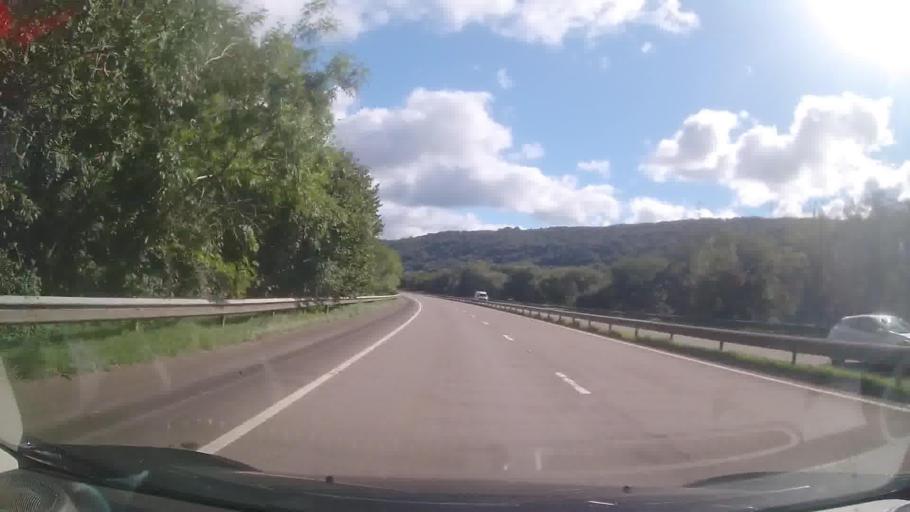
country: GB
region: Wales
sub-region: Neath Port Talbot
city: Neath
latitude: 51.6818
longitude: -3.7647
